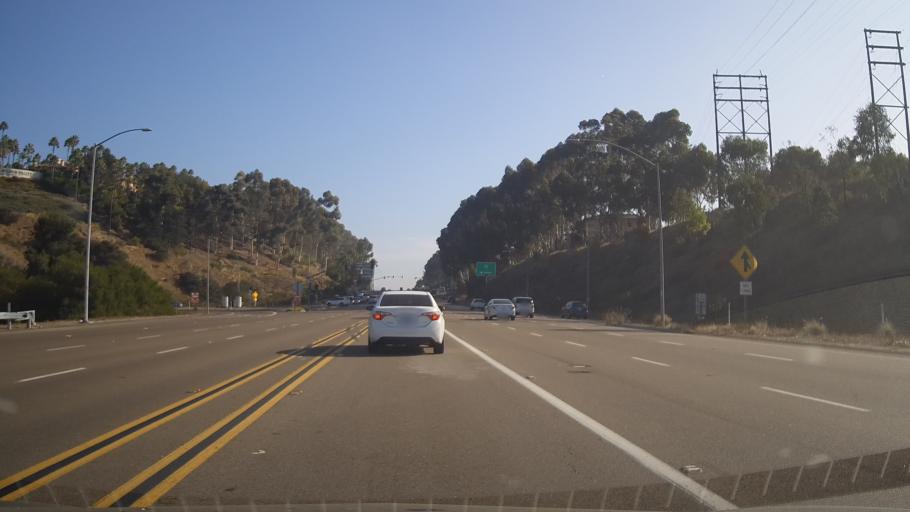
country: US
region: California
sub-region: San Diego County
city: San Diego
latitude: 32.7880
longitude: -117.1117
